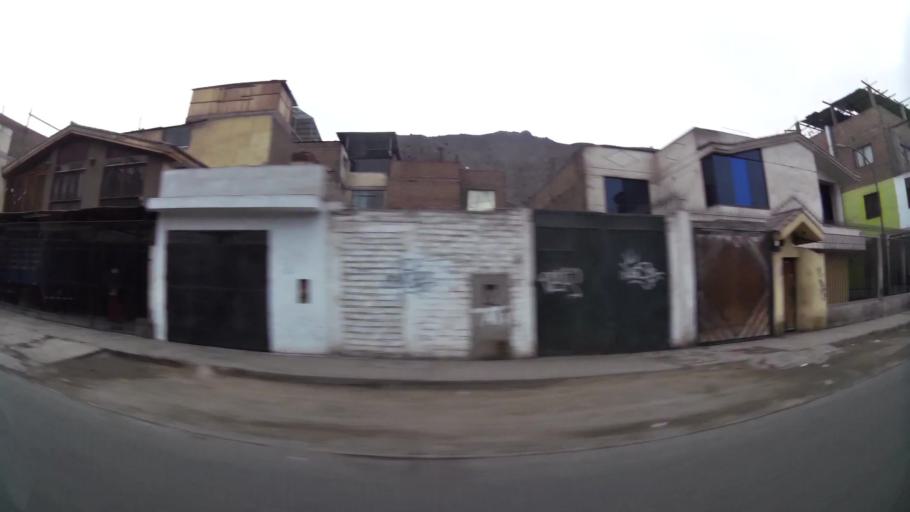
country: PE
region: Lima
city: Lima
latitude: -12.0148
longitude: -76.9871
